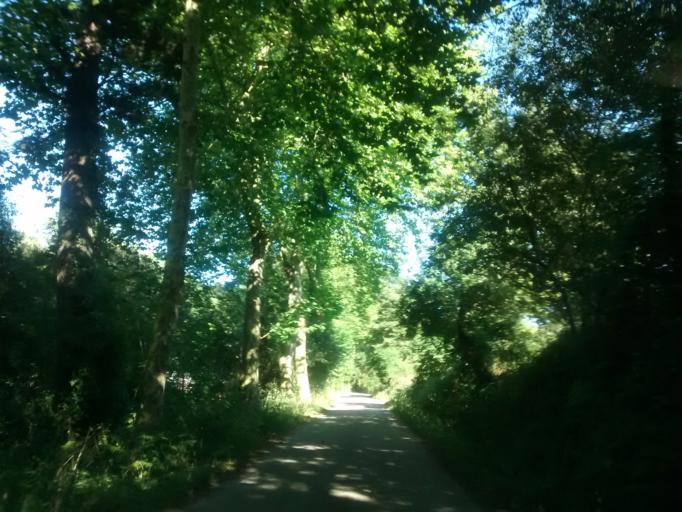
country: ES
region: Cantabria
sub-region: Provincia de Cantabria
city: Entrambasaguas
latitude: 43.3955
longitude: -3.7059
